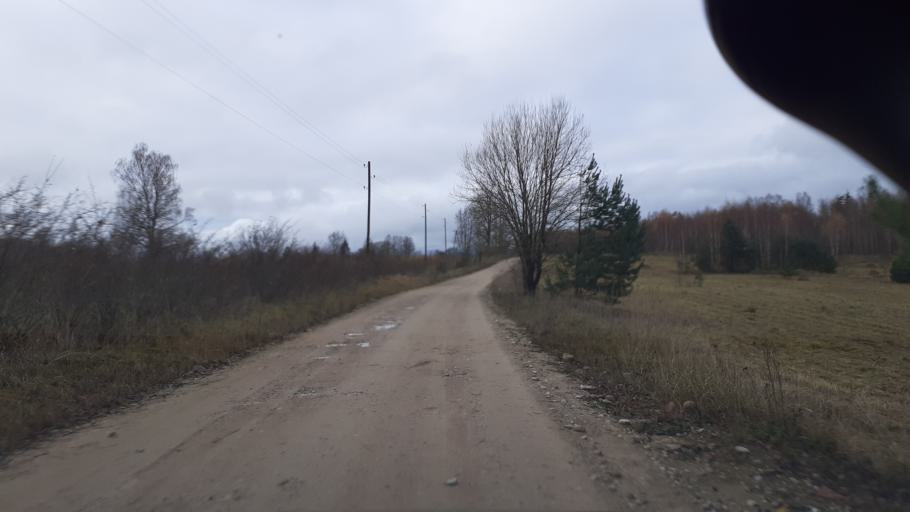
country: LV
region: Kuldigas Rajons
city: Kuldiga
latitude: 57.0406
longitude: 21.8779
